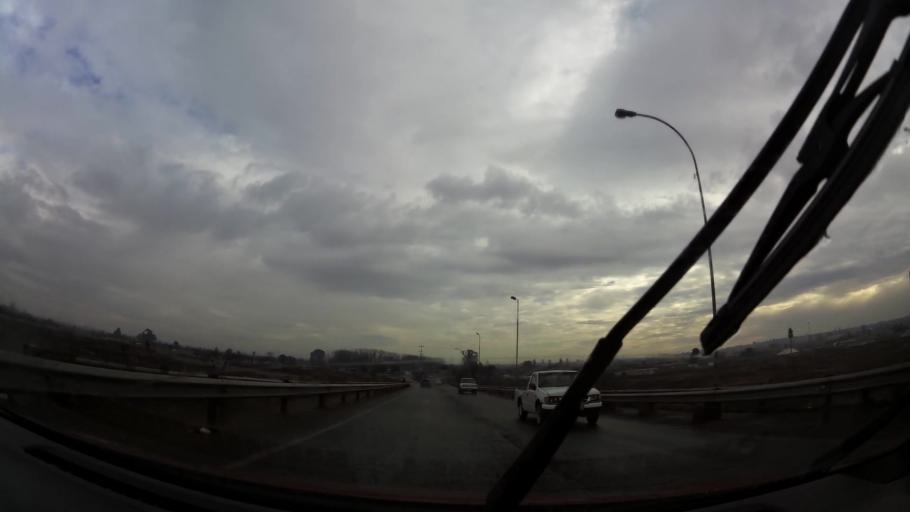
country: ZA
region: Gauteng
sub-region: City of Johannesburg Metropolitan Municipality
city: Soweto
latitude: -26.2932
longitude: 27.8455
